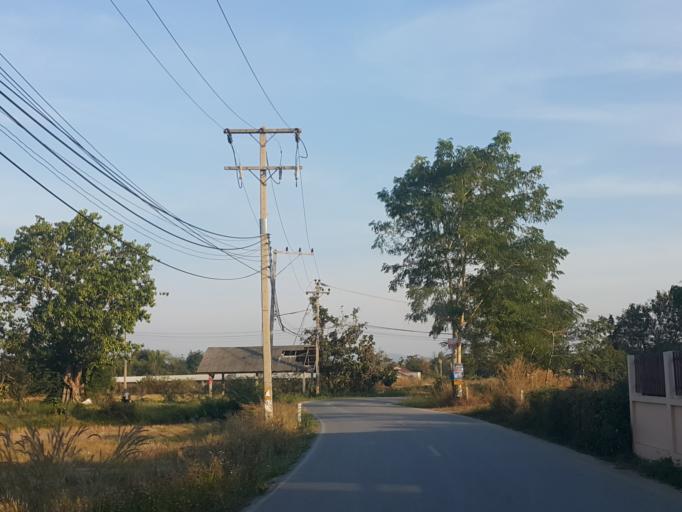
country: TH
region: Chiang Mai
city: San Sai
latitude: 18.8281
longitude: 99.0821
